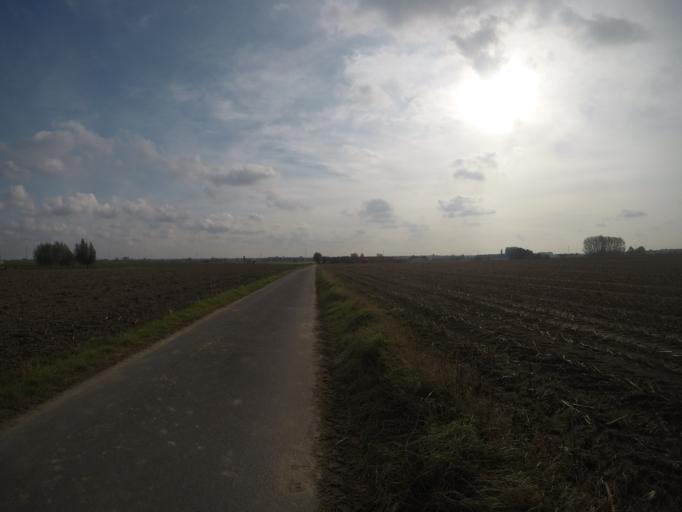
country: BE
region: Flanders
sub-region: Provincie West-Vlaanderen
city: Moorslede
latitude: 50.8404
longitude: 3.0727
